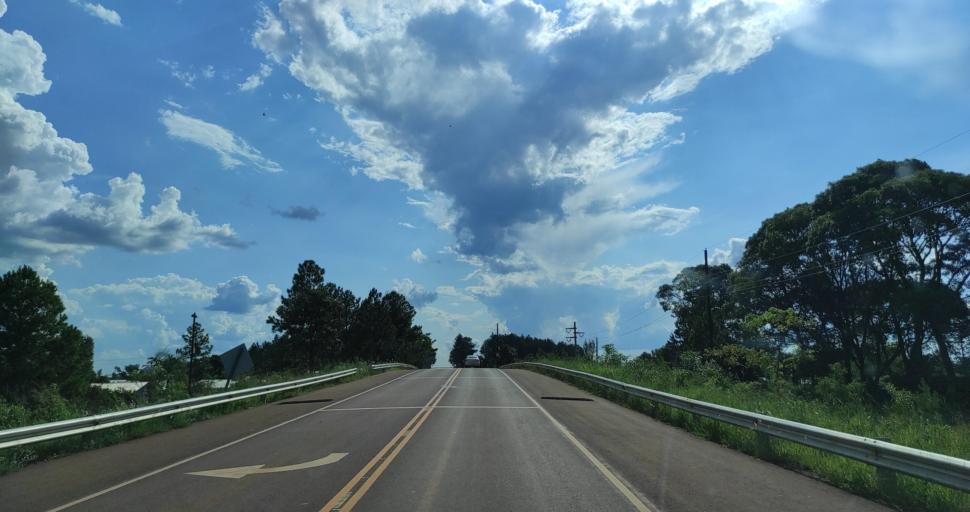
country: AR
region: Misiones
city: Bernardo de Irigoyen
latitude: -26.2960
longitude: -53.7915
